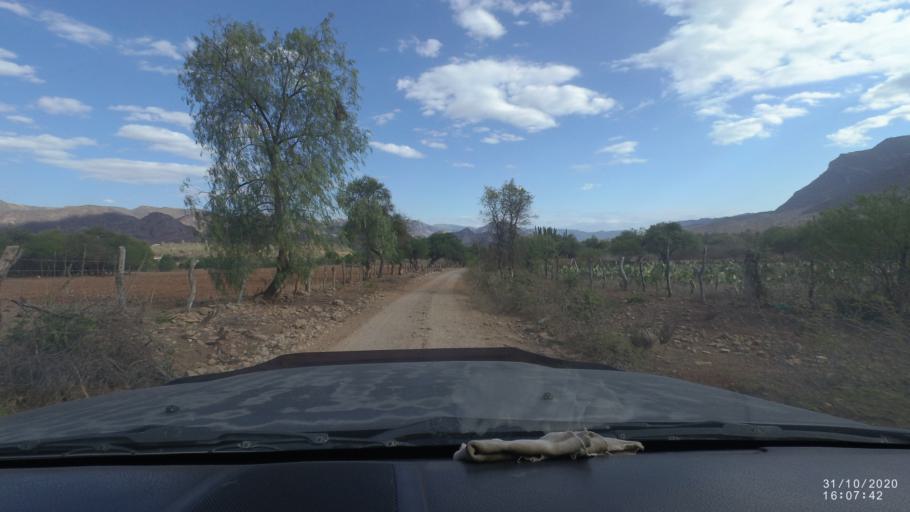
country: BO
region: Chuquisaca
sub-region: Provincia Zudanez
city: Mojocoya
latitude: -18.3817
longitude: -64.6440
